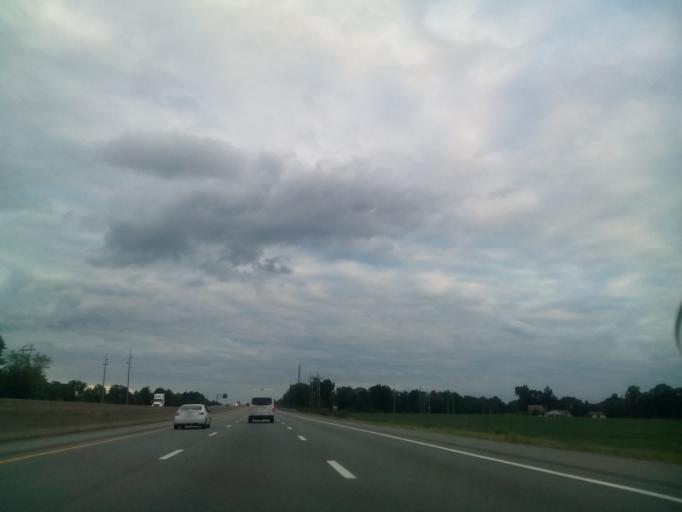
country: US
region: Ohio
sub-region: Trumbull County
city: Newton Falls
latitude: 41.1925
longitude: -80.9410
